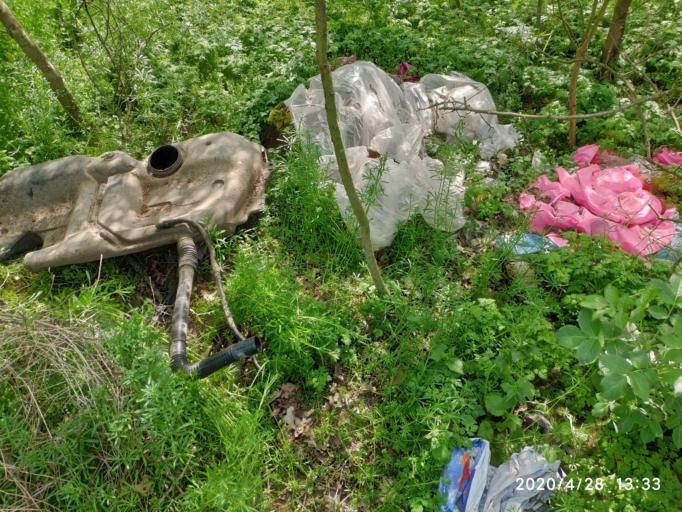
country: PL
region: Lubusz
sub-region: Powiat krosnienski
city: Krosno Odrzanskie
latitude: 52.0393
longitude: 15.0799
